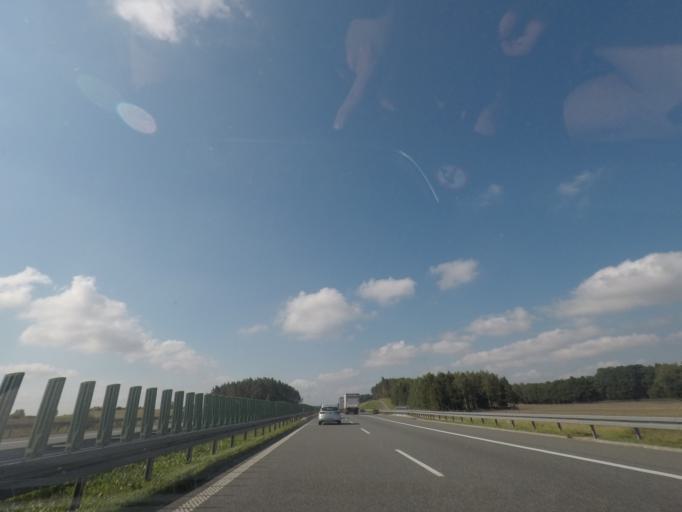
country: PL
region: Pomeranian Voivodeship
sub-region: Powiat tczewski
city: Pelplin
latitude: 53.9038
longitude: 18.6425
